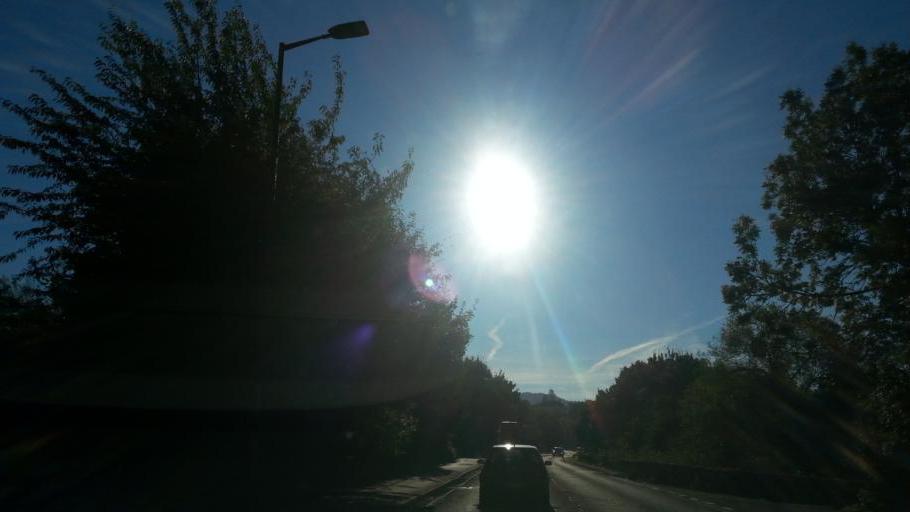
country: GB
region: England
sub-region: Herefordshire
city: Ross on Wye
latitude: 51.9145
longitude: -2.5964
